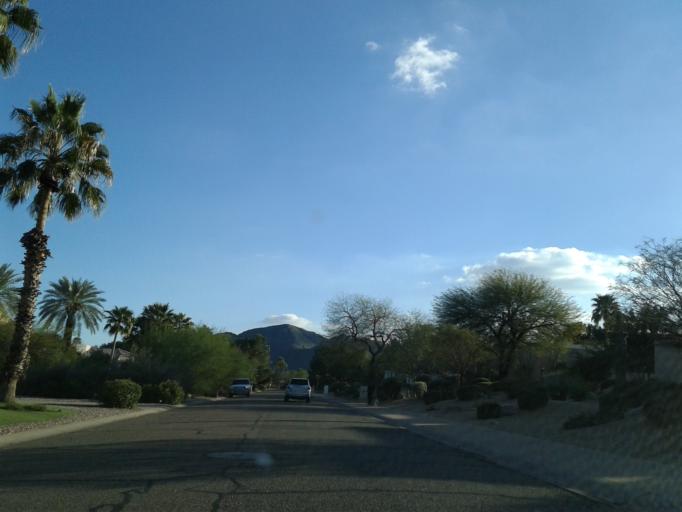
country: US
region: Arizona
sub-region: Maricopa County
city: Paradise Valley
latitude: 33.5743
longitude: -111.9584
